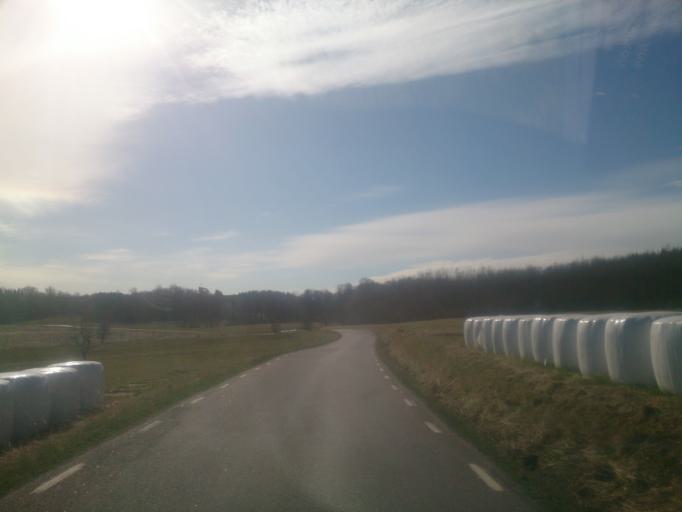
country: SE
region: OEstergoetland
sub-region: Linkopings Kommun
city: Sturefors
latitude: 58.2968
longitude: 15.8485
